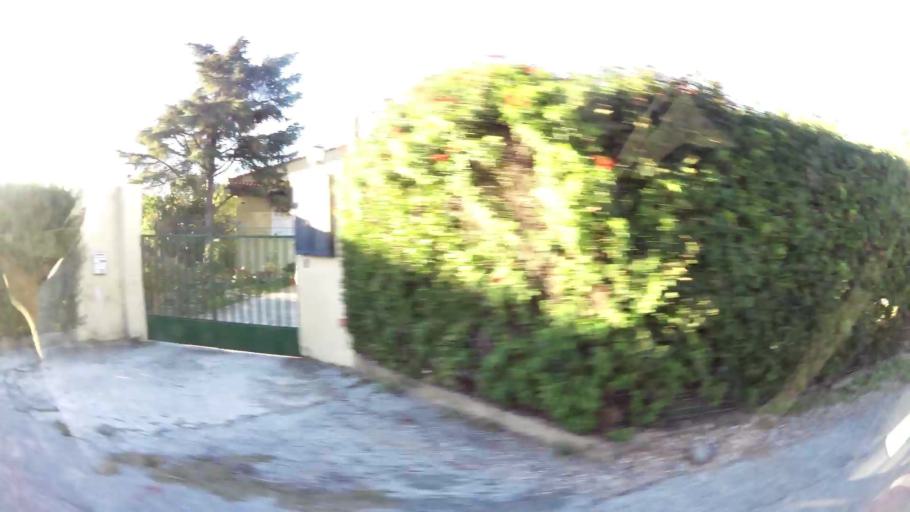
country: GR
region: Attica
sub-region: Nomarchia Anatolikis Attikis
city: Pallini
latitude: 38.0013
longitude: 23.8660
